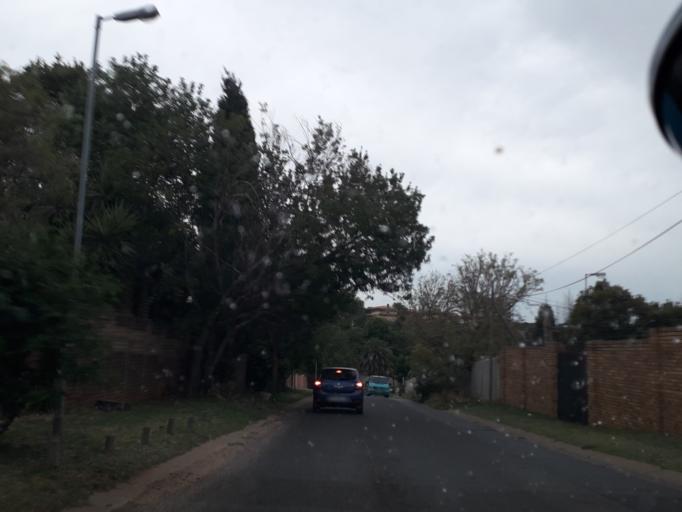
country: ZA
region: Gauteng
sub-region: City of Johannesburg Metropolitan Municipality
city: Johannesburg
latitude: -26.0925
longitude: 28.0122
